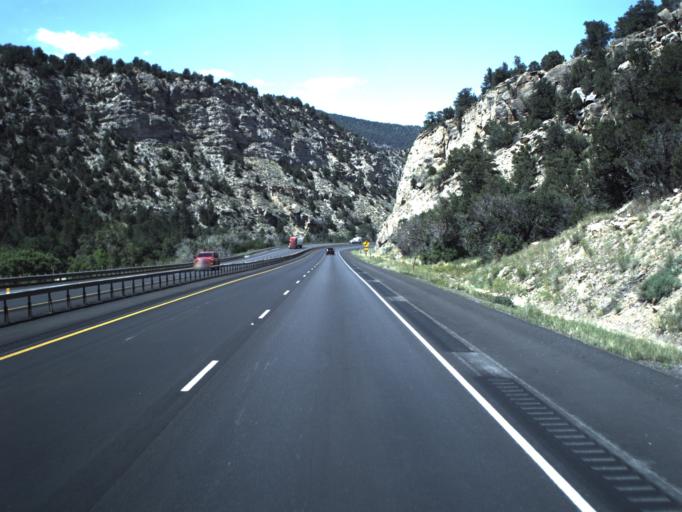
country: US
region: Utah
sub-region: Sevier County
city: Salina
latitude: 38.8971
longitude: -111.6293
